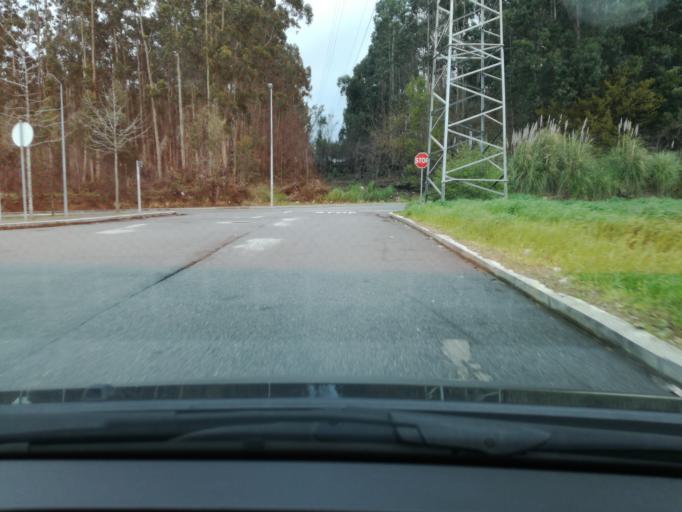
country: PT
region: Porto
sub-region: Maia
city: Anta
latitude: 41.2552
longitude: -8.6373
